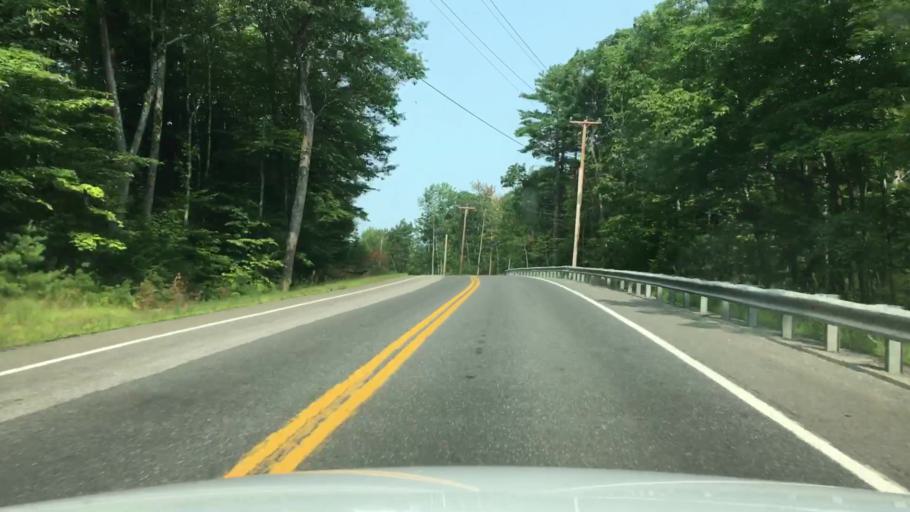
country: US
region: Maine
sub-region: Kennebec County
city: Augusta
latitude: 44.3159
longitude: -69.7210
